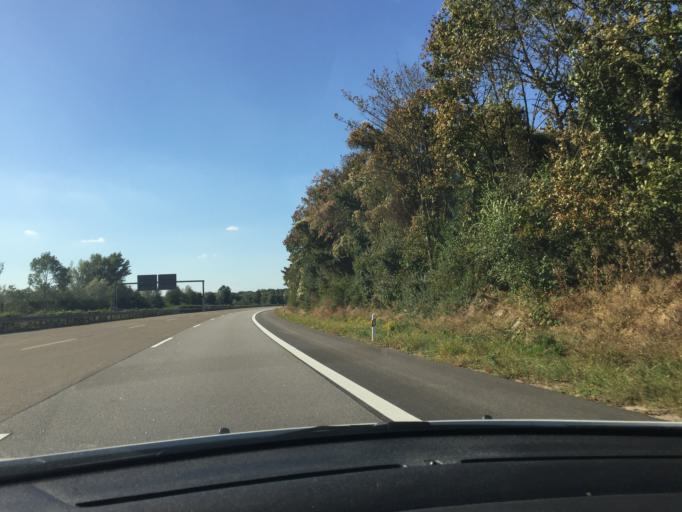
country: DE
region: Hesse
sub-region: Regierungsbezirk Darmstadt
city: Maintal
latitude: 50.1426
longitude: 8.7942
